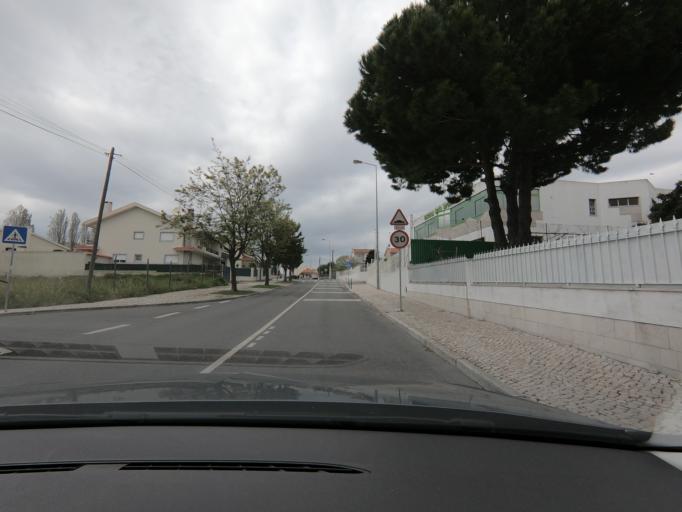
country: PT
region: Lisbon
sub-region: Cascais
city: Sao Domingos de Rana
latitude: 38.7000
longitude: -9.3371
